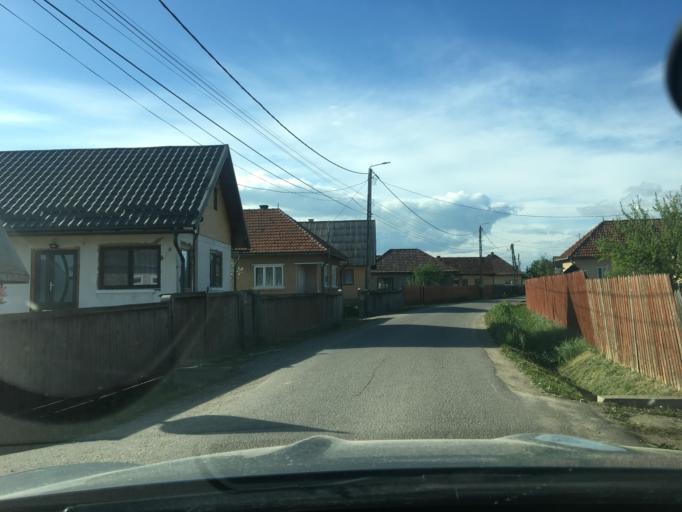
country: RO
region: Harghita
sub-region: Comuna Ditrau
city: Ditrau
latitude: 46.7971
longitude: 25.4869
